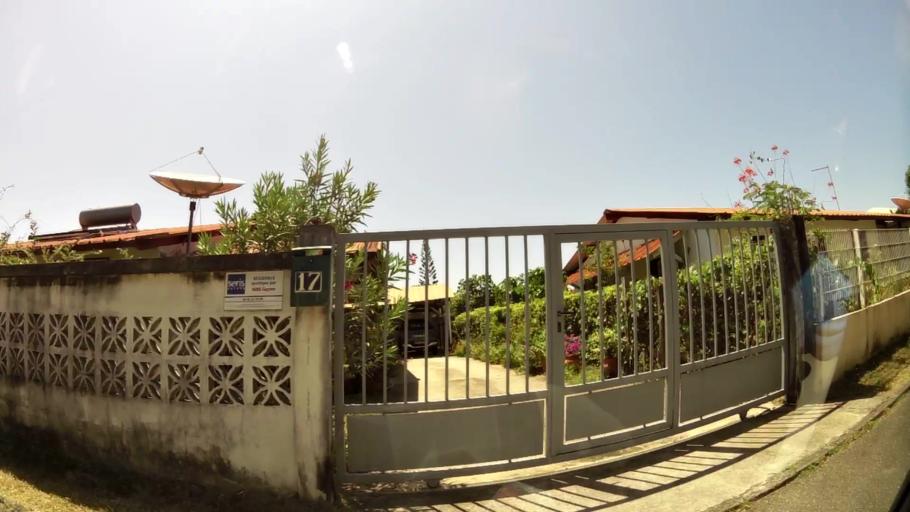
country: GF
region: Guyane
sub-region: Guyane
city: Kourou
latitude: 5.1698
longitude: -52.6522
